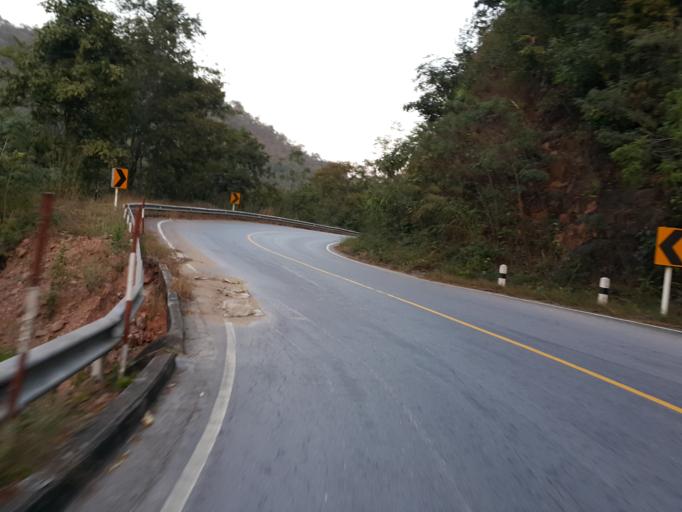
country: TH
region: Lampang
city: Thoen
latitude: 17.6845
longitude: 99.0787
